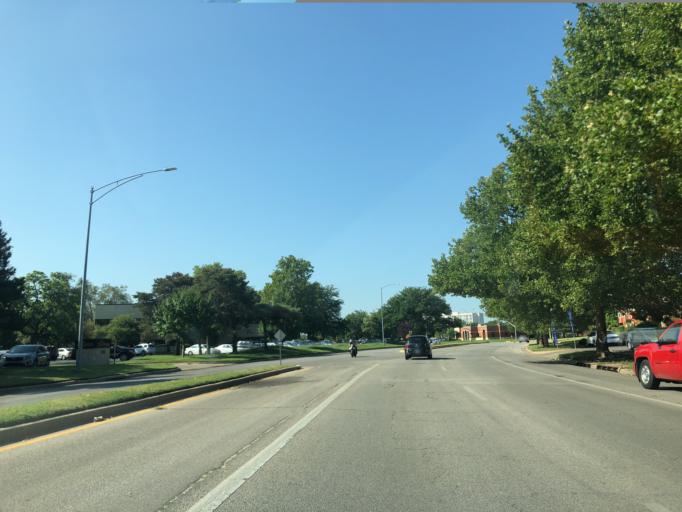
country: US
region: Kansas
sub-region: Sedgwick County
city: Wichita
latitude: 37.6953
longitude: -97.3412
